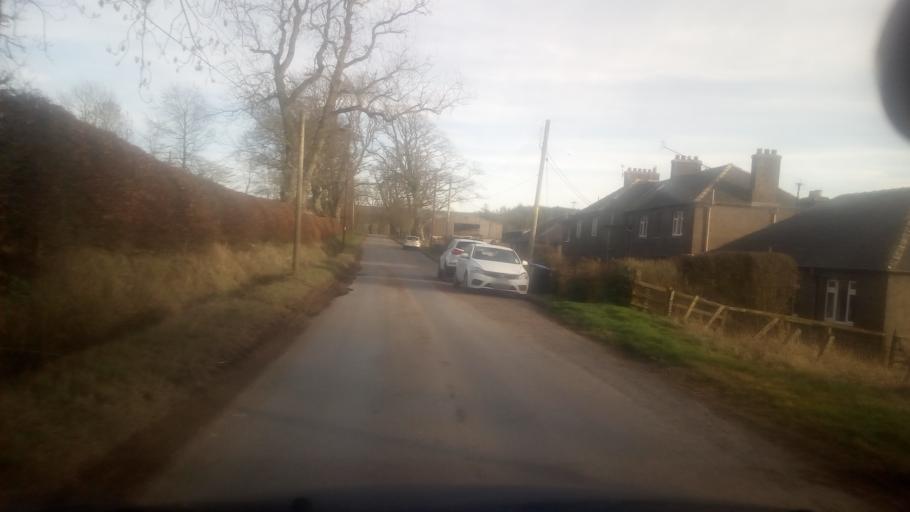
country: GB
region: Scotland
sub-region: The Scottish Borders
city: Jedburgh
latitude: 55.4094
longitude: -2.6087
